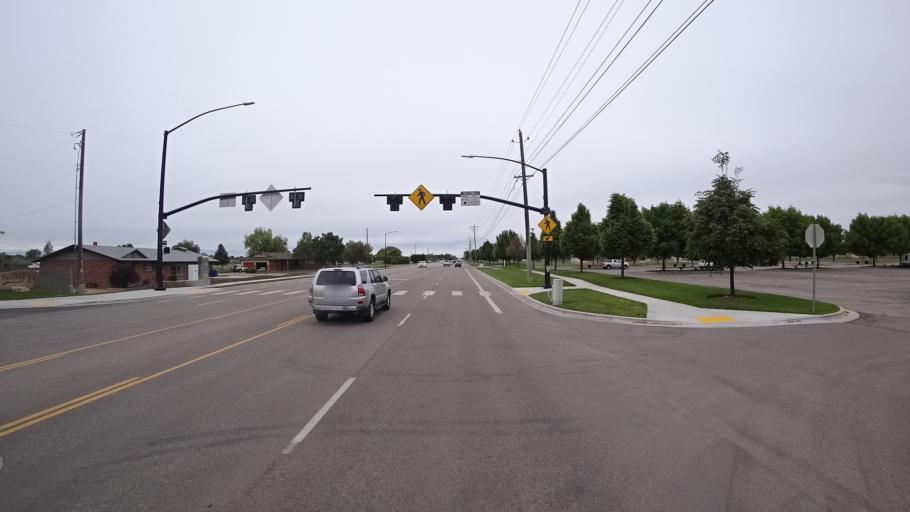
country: US
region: Idaho
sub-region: Ada County
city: Meridian
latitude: 43.6339
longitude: -116.3978
